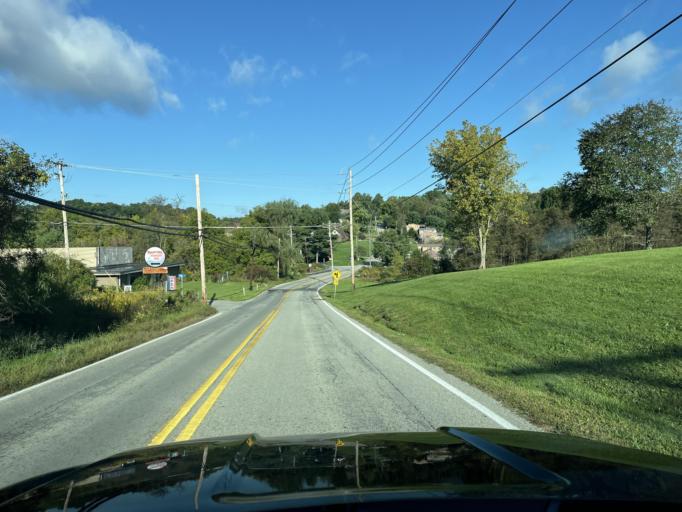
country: US
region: Pennsylvania
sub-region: Fayette County
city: South Uniontown
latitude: 39.8825
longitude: -79.7507
